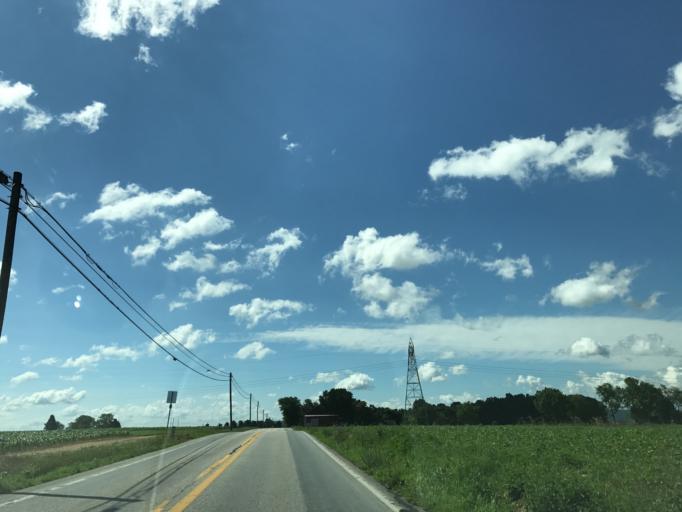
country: US
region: Pennsylvania
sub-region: Lancaster County
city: Rheems
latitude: 40.1193
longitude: -76.5965
